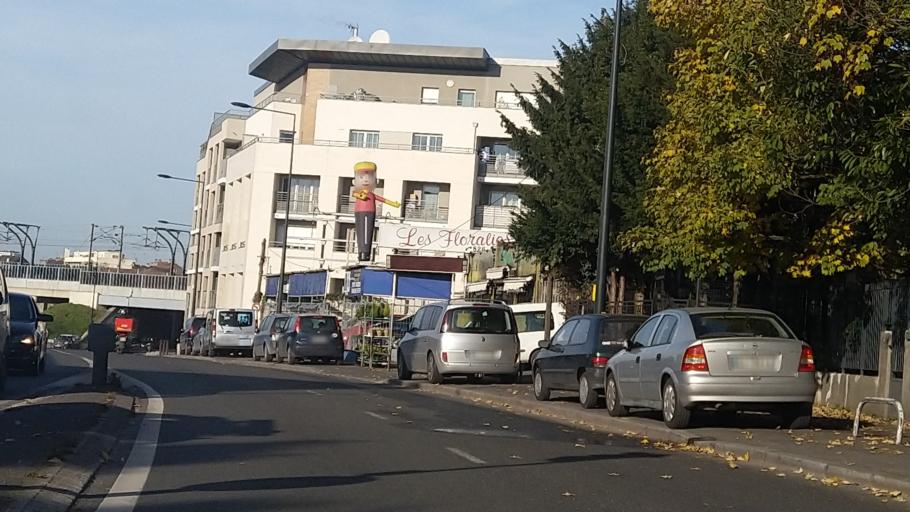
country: FR
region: Ile-de-France
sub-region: Departement de Seine-Saint-Denis
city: Stains
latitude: 48.9570
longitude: 2.3832
